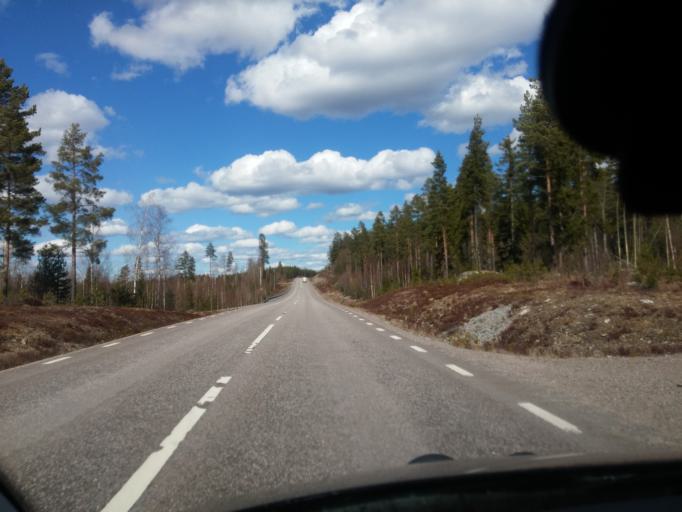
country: SE
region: Gaevleborg
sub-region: Ovanakers Kommun
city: Edsbyn
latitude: 61.2405
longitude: 15.8819
